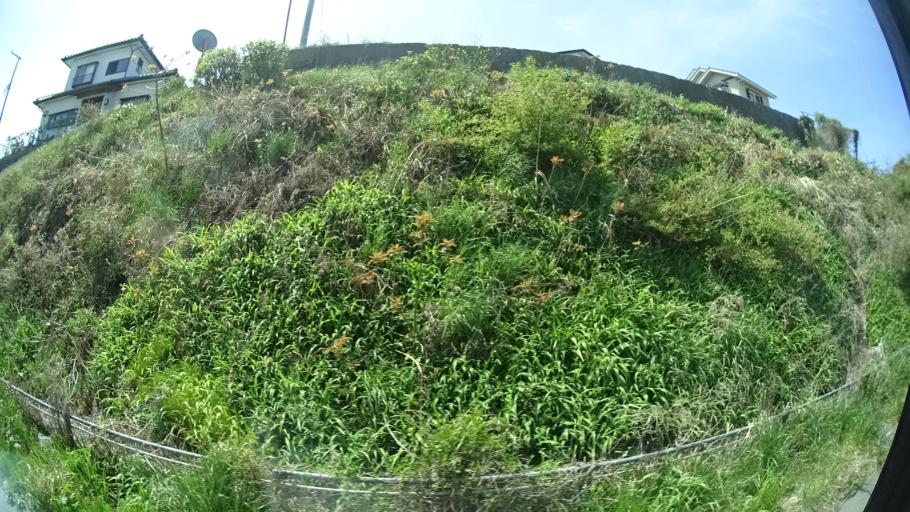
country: JP
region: Iwate
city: Ofunato
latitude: 39.0472
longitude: 141.7223
